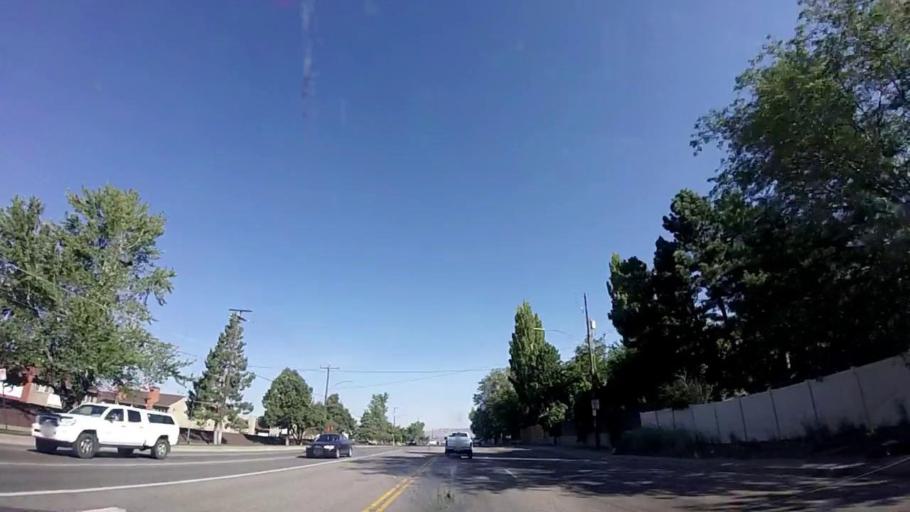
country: US
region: Utah
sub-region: Salt Lake County
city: Canyon Rim
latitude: 40.7218
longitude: -111.8120
